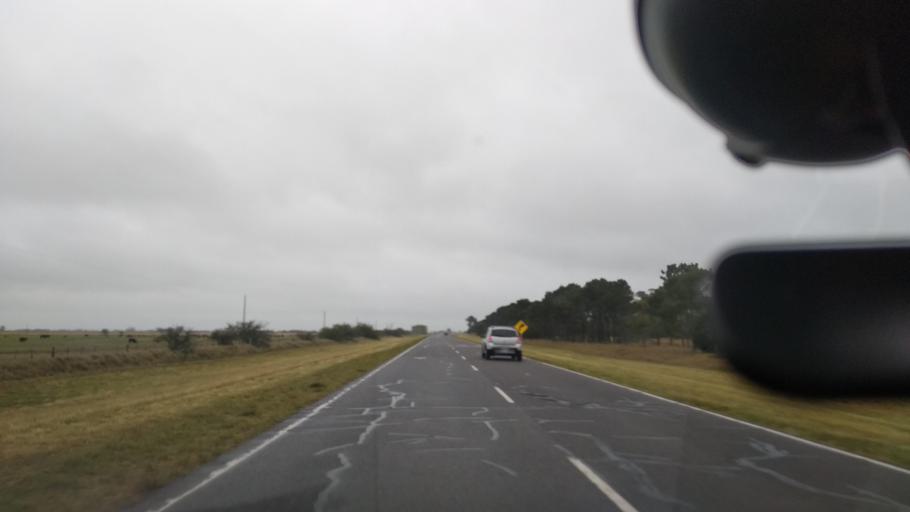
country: AR
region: Buenos Aires
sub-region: Partido de Dolores
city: Dolores
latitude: -36.0519
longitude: -57.4440
